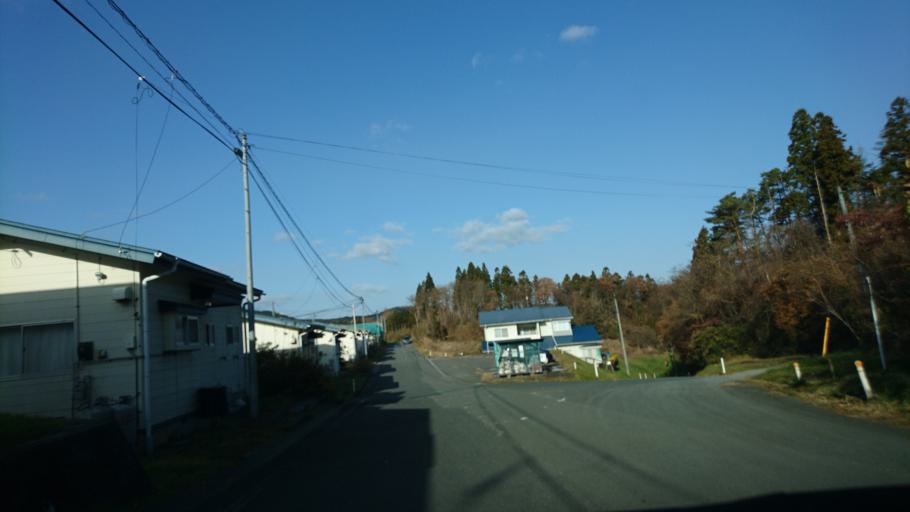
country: JP
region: Iwate
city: Ichinoseki
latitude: 38.8688
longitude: 141.3484
